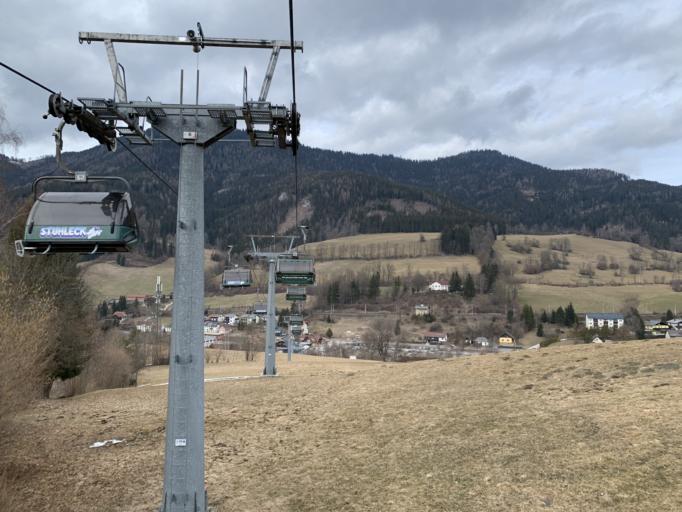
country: AT
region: Styria
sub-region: Politischer Bezirk Bruck-Muerzzuschlag
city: Spital am Semmering
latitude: 47.6114
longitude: 15.7586
